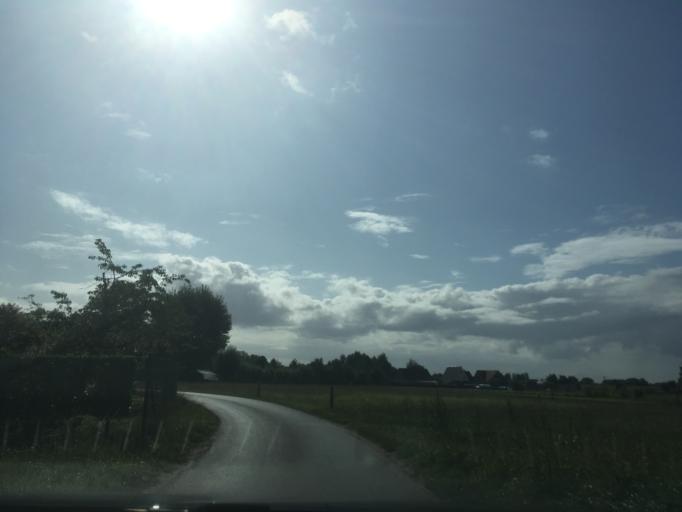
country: BE
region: Flanders
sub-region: Provincie West-Vlaanderen
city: Staden
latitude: 50.9985
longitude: 3.0303
